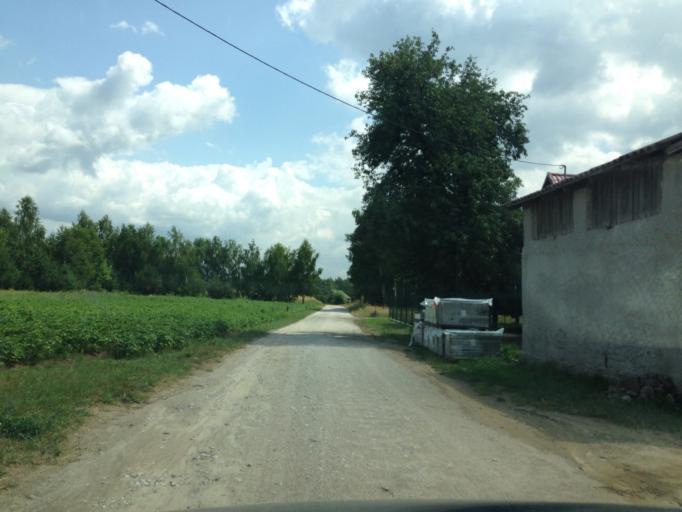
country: PL
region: Kujawsko-Pomorskie
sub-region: Powiat brodnicki
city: Gorzno
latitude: 53.2270
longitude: 19.6423
